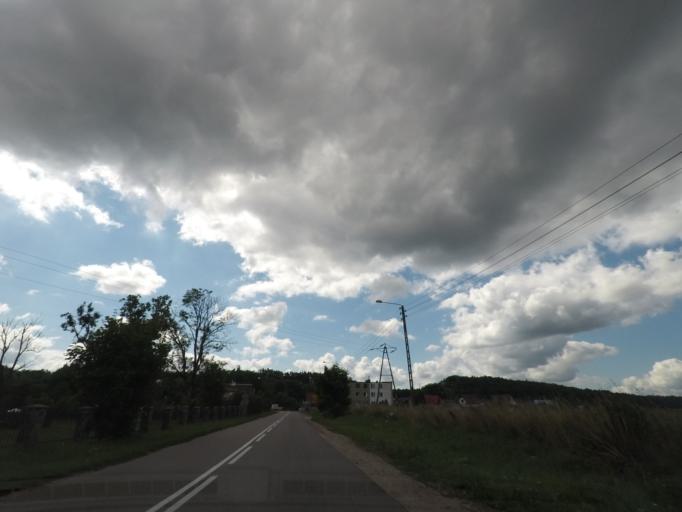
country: PL
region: Pomeranian Voivodeship
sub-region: Powiat wejherowski
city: Leczyce
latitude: 54.5757
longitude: 17.8653
